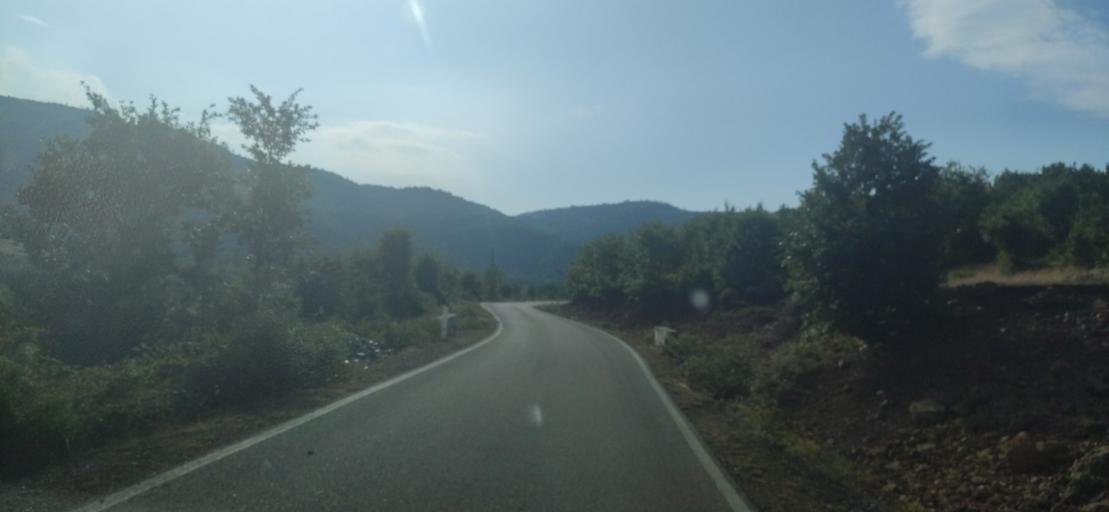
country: AL
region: Shkoder
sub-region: Rrethi i Pukes
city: Iballe
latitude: 42.1821
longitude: 19.9978
